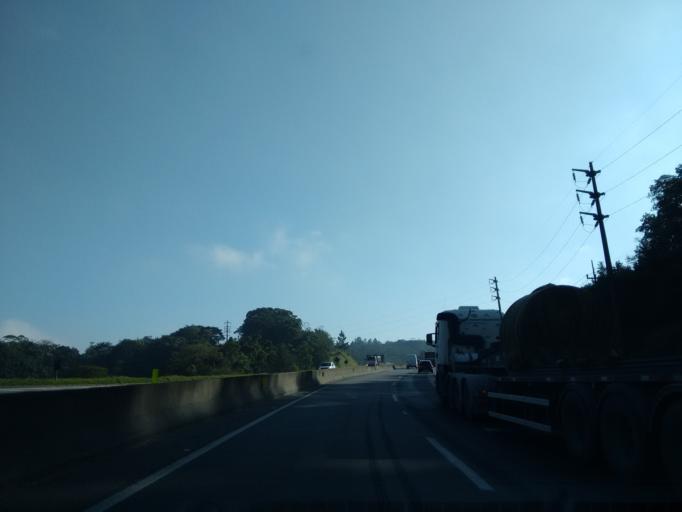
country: BR
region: Santa Catarina
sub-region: Joinville
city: Joinville
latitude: -26.3161
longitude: -48.8736
